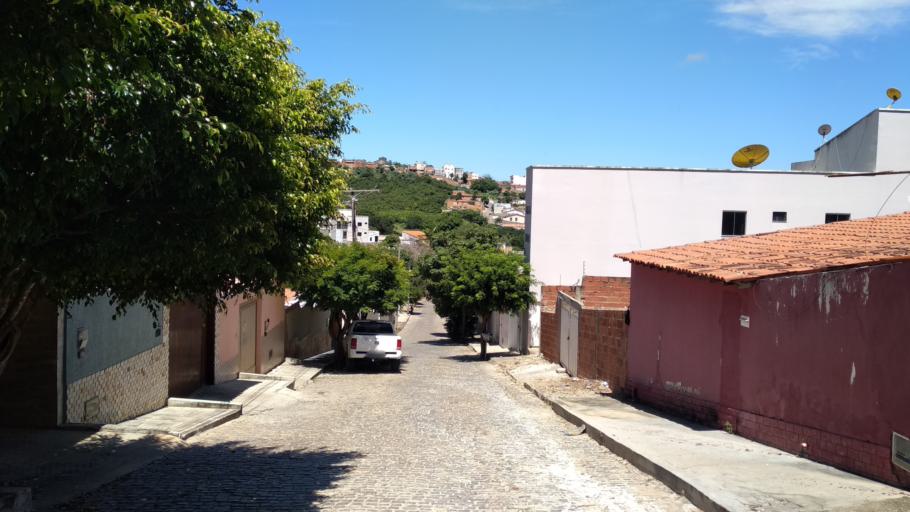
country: BR
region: Bahia
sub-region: Caetite
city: Caetite
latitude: -14.0743
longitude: -42.4824
